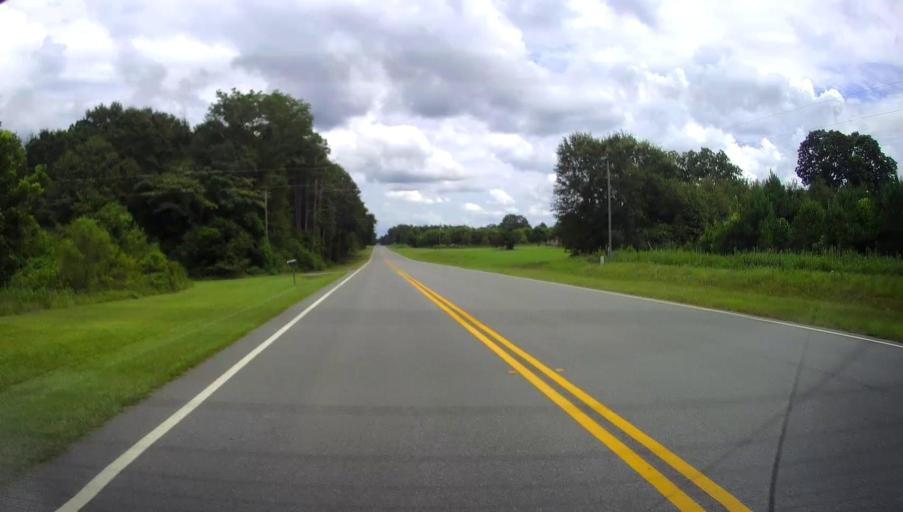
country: US
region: Georgia
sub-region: Macon County
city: Oglethorpe
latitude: 32.2797
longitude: -84.1405
